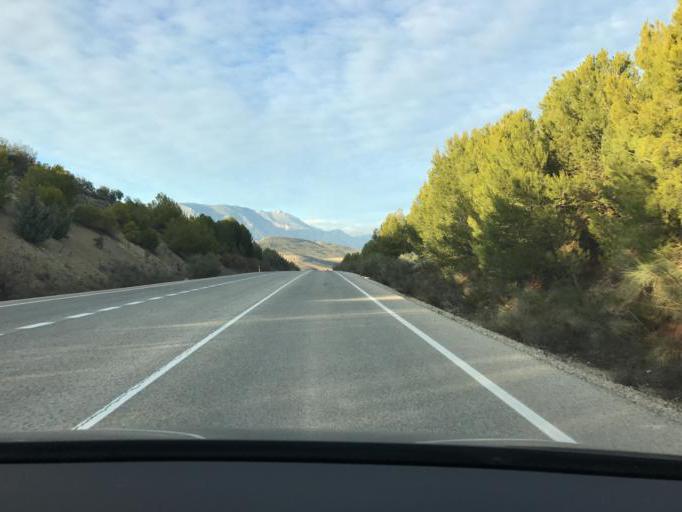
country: ES
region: Andalusia
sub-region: Provincia de Jaen
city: Huelma
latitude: 37.6274
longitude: -3.4012
